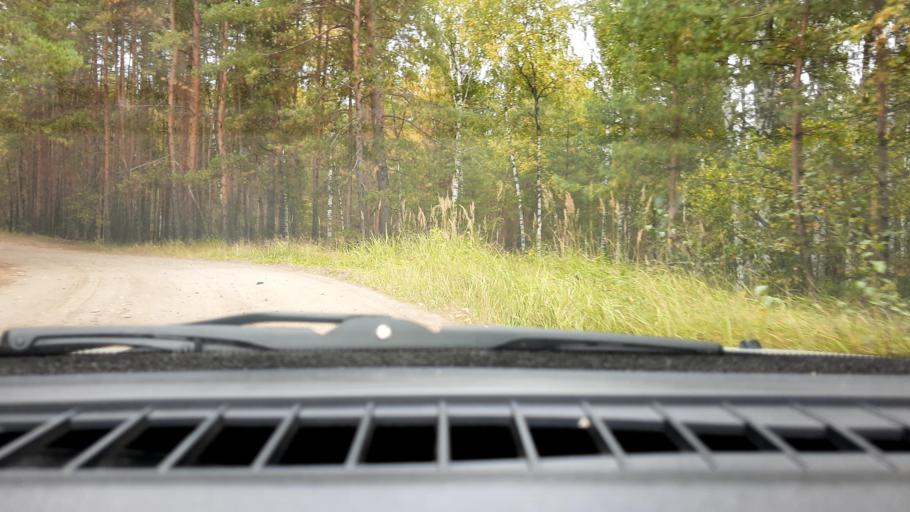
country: RU
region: Nizjnij Novgorod
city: Gorbatovka
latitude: 56.3150
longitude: 43.6960
